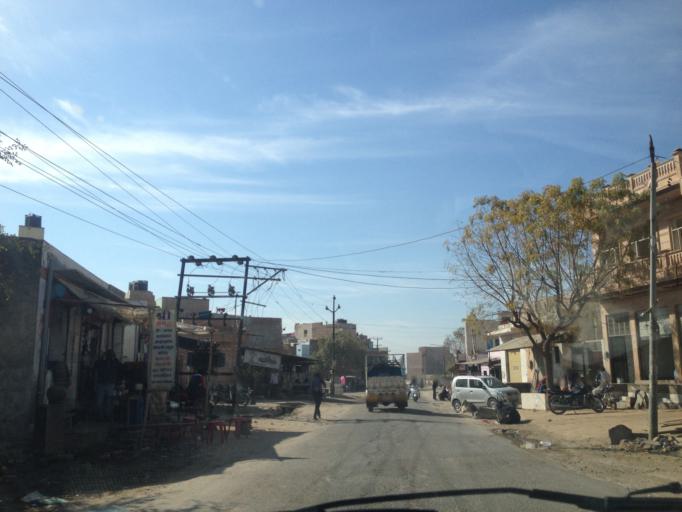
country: IN
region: Rajasthan
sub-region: Nagaur
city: Merta
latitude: 26.6454
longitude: 74.0268
